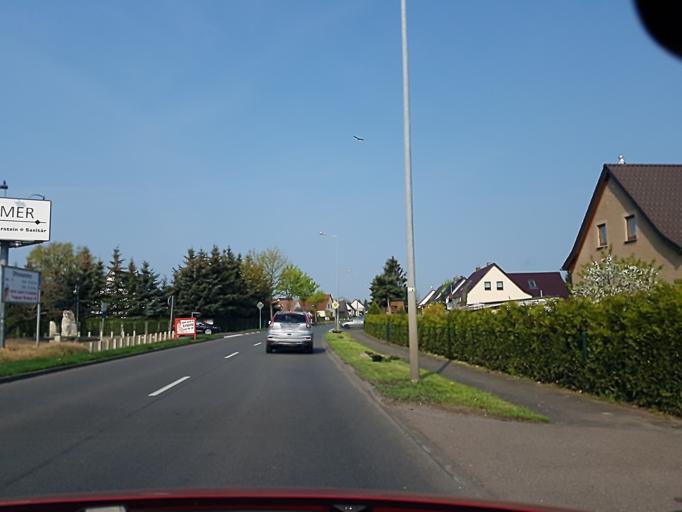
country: DE
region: Saxony
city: Beilrode
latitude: 51.5810
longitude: 13.0468
